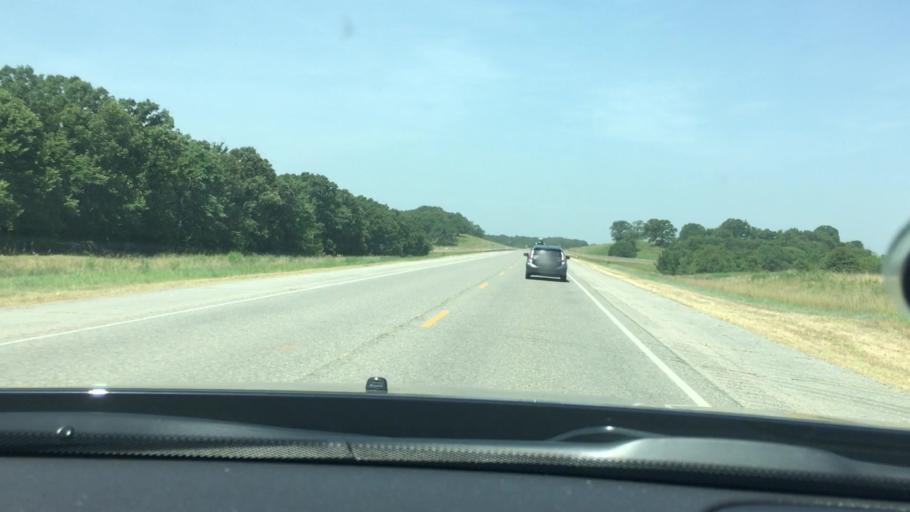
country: US
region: Oklahoma
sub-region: Coal County
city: Coalgate
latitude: 34.6001
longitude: -96.3502
